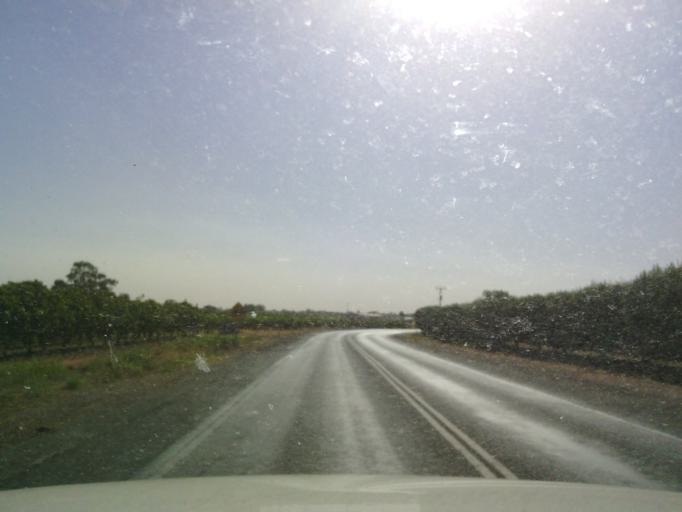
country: AU
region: South Australia
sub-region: Berri and Barmera
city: Berri
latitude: -34.2811
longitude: 140.5769
